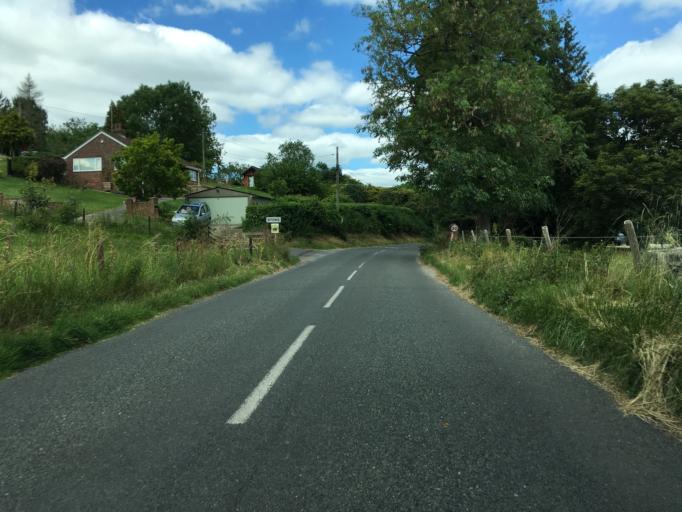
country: GB
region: England
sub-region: Hampshire
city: Andover
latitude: 51.2628
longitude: -1.4220
